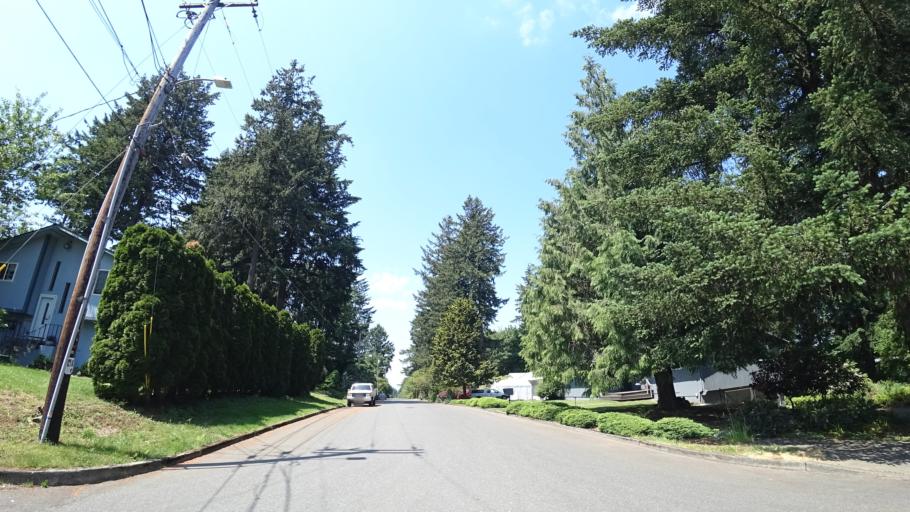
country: US
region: Oregon
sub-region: Washington County
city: Metzger
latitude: 45.4411
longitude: -122.7231
